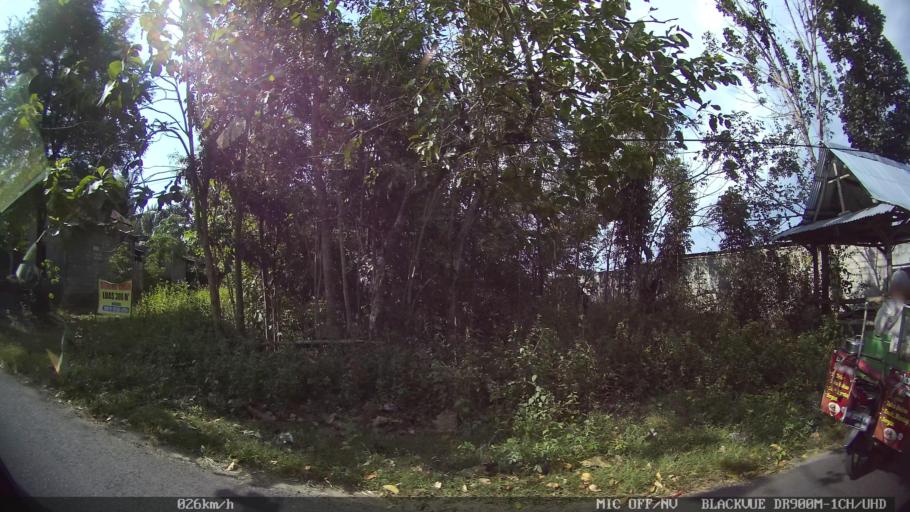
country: ID
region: Daerah Istimewa Yogyakarta
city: Kasihan
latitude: -7.8537
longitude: 110.3013
